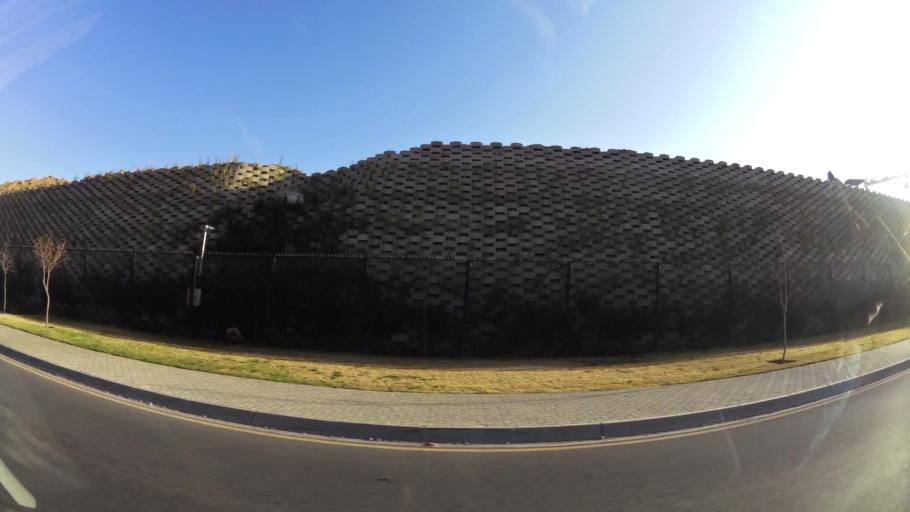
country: ZA
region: Gauteng
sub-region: City of Johannesburg Metropolitan Municipality
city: Midrand
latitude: -26.0267
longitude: 28.1257
